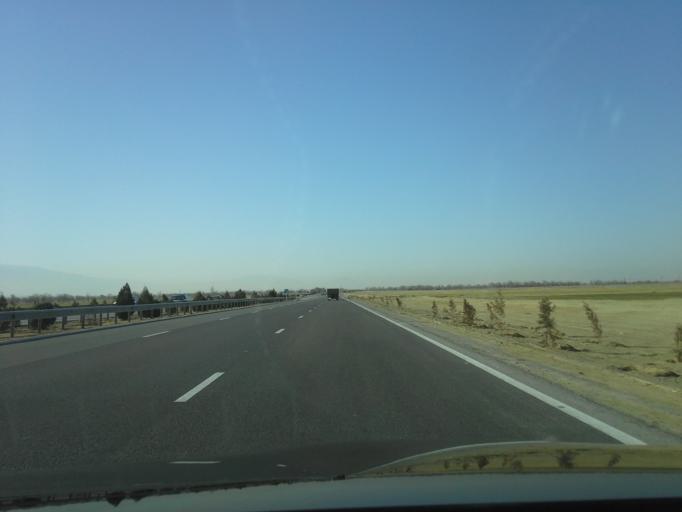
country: TM
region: Ahal
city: Annau
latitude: 37.8973
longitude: 58.5939
